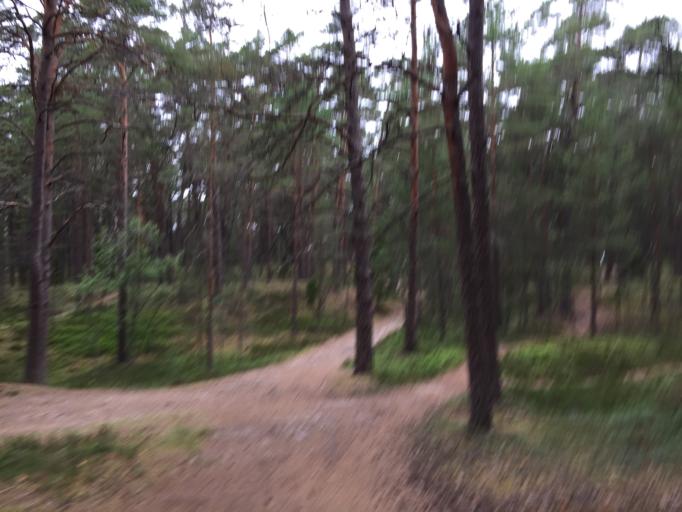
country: LV
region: Carnikava
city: Carnikava
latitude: 57.1230
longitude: 24.2158
